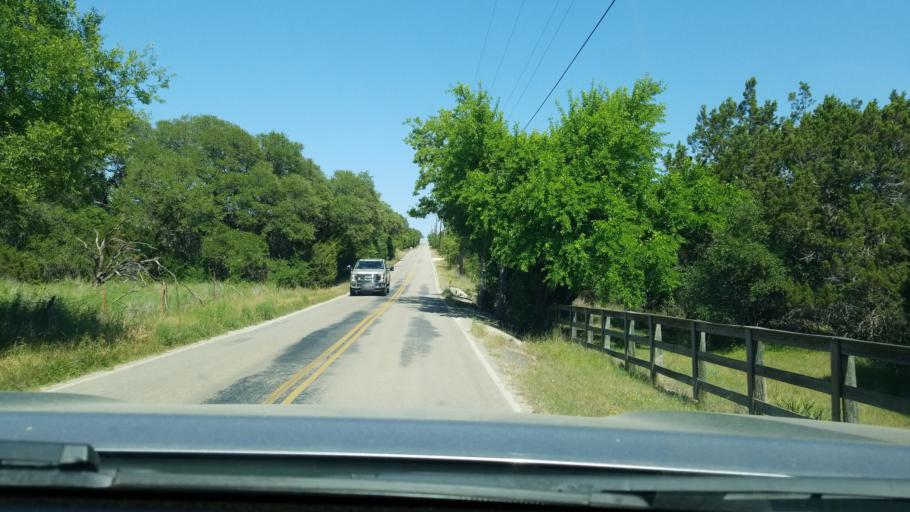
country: US
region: Texas
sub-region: Comal County
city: Bulverde
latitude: 29.7591
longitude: -98.4948
